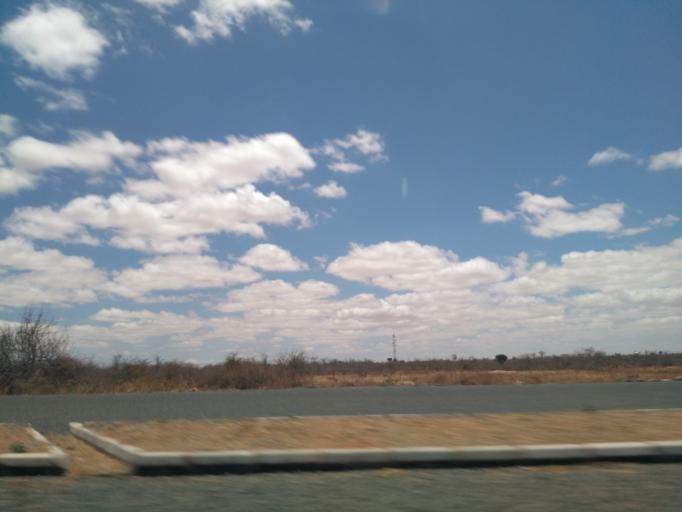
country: TZ
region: Dodoma
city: Kisasa
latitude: -6.1691
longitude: 35.8433
